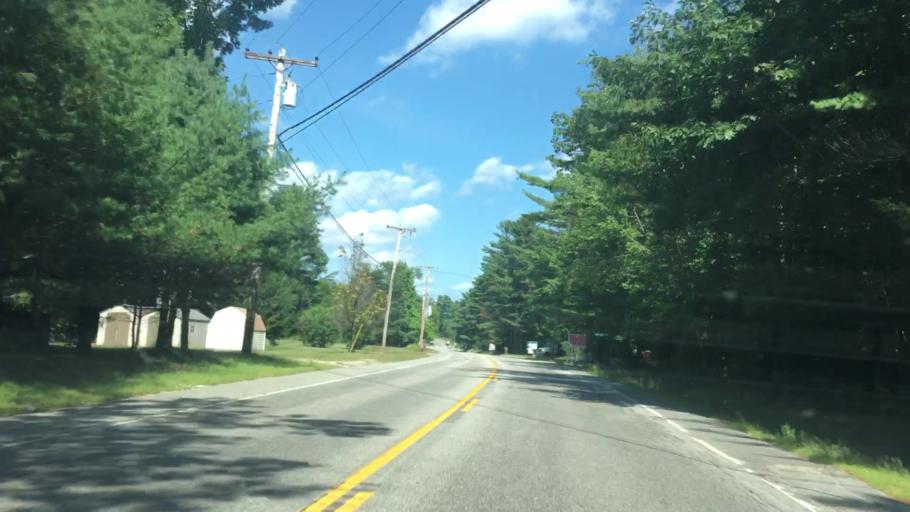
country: US
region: Maine
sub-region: Cumberland County
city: New Gloucester
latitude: 43.9209
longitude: -70.3142
